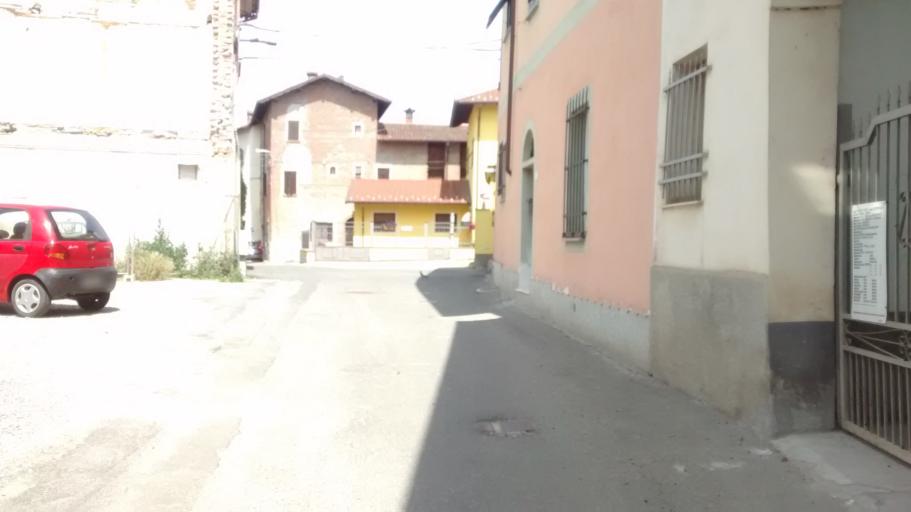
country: IT
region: Piedmont
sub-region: Provincia di Alessandria
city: Capriata d'Orba
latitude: 44.7305
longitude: 8.6896
